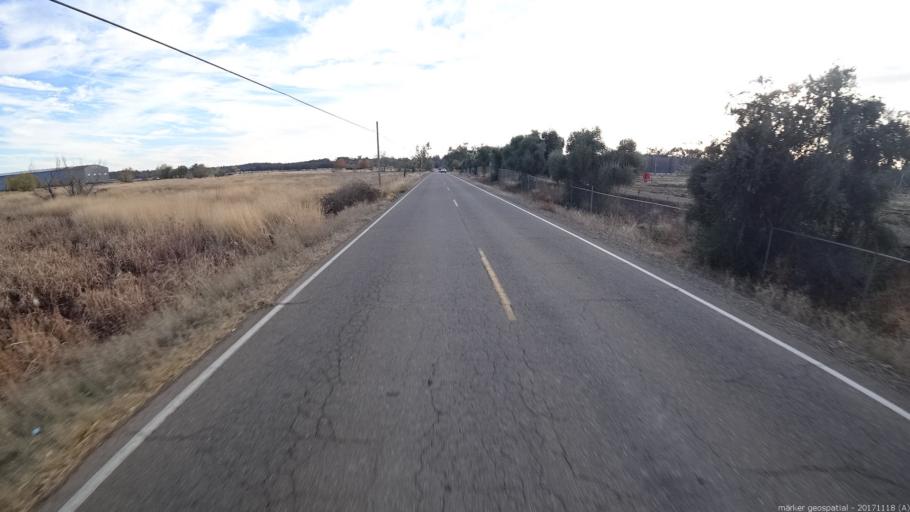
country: US
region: California
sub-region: Shasta County
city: Anderson
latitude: 40.4281
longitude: -122.2735
